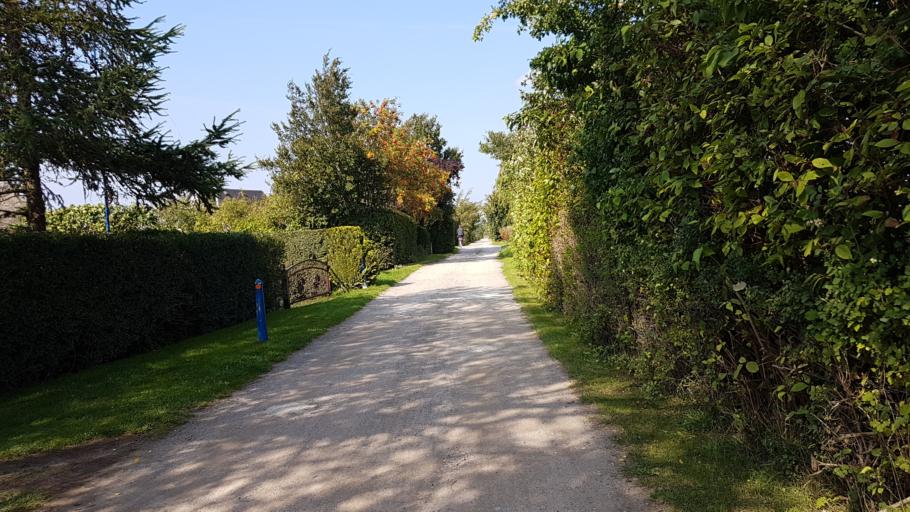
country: DE
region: Mecklenburg-Vorpommern
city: Glowe
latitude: 54.5466
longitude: 13.5053
